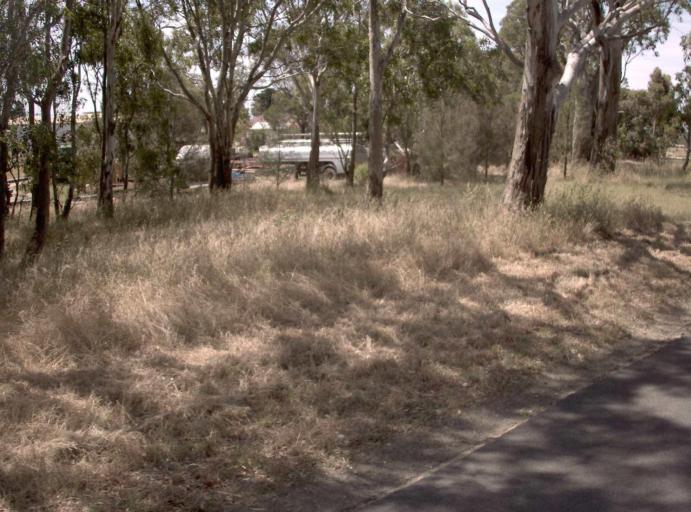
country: AU
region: Victoria
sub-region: Latrobe
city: Traralgon
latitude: -38.1672
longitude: 146.6982
